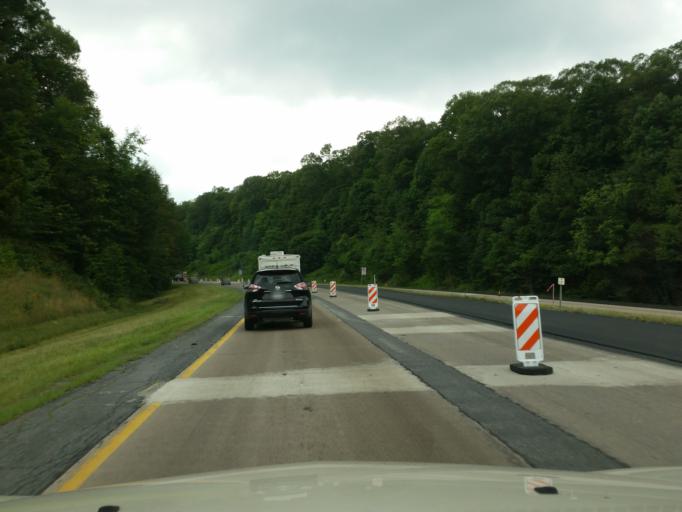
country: US
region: Pennsylvania
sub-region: Perry County
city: Newport
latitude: 40.5706
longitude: -77.2404
